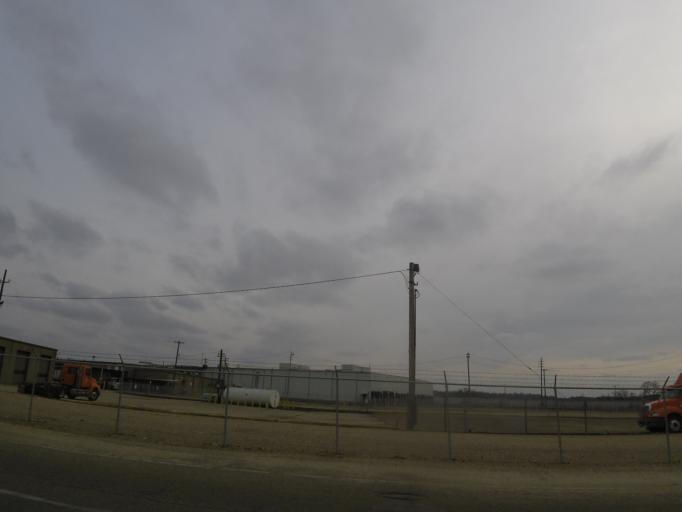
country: US
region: Alabama
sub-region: Montgomery County
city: Montgomery
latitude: 32.4023
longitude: -86.3081
